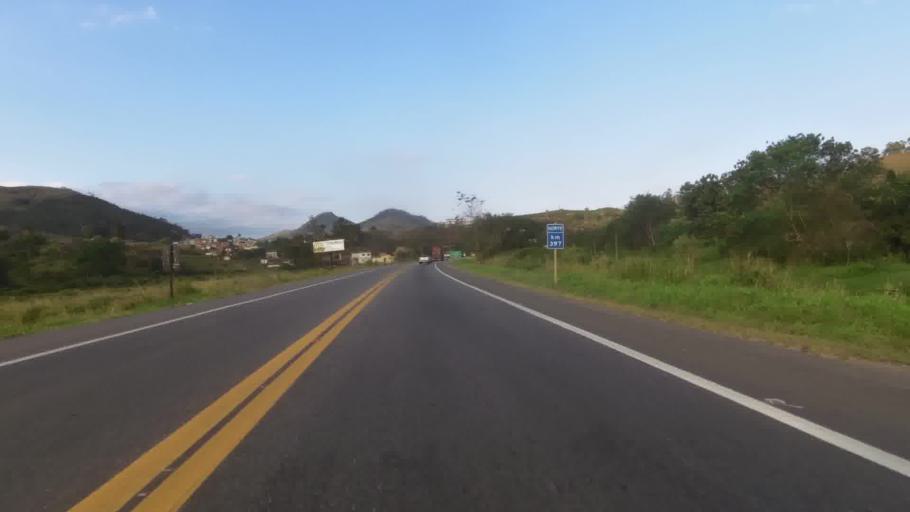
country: BR
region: Espirito Santo
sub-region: Rio Novo Do Sul
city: Rio Novo do Sul
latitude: -20.8732
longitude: -40.9498
